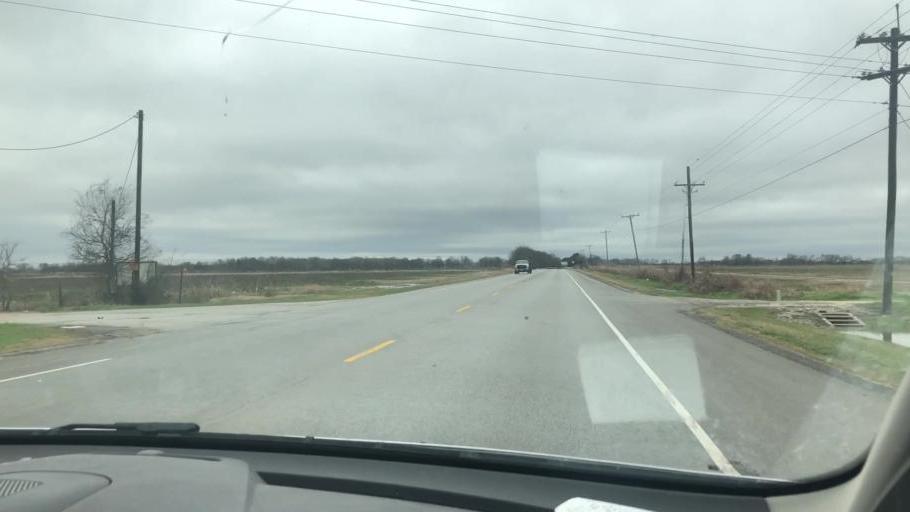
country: US
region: Texas
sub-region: Matagorda County
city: Bay City
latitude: 29.0683
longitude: -95.9711
